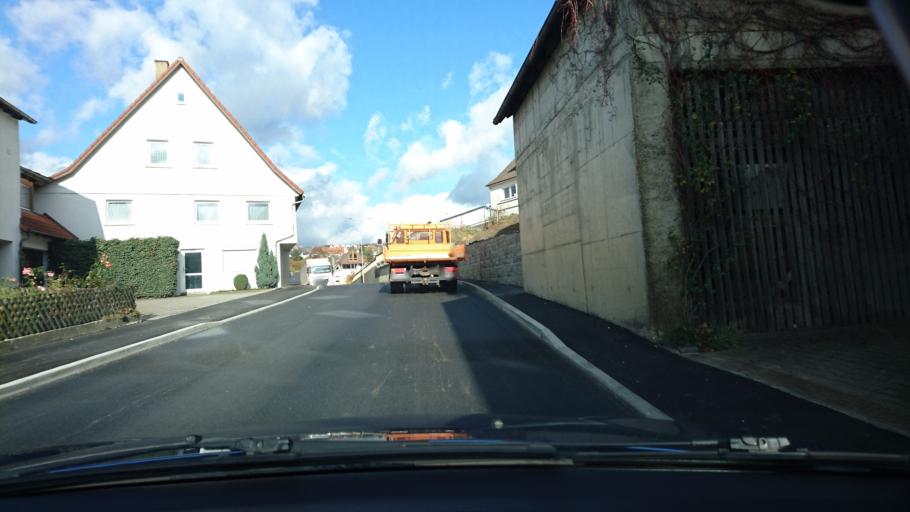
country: DE
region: Baden-Wuerttemberg
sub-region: Regierungsbezirk Stuttgart
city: Huttlingen
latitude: 48.8904
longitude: 10.1007
